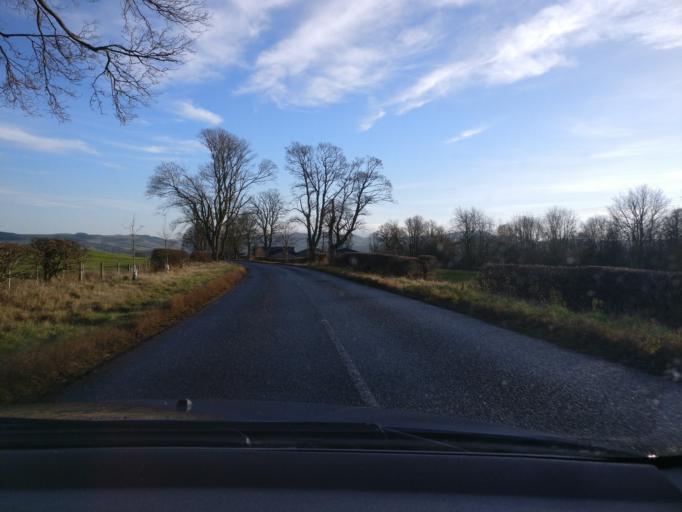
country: GB
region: Scotland
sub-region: The Scottish Borders
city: Kelso
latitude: 55.5273
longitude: -2.4231
